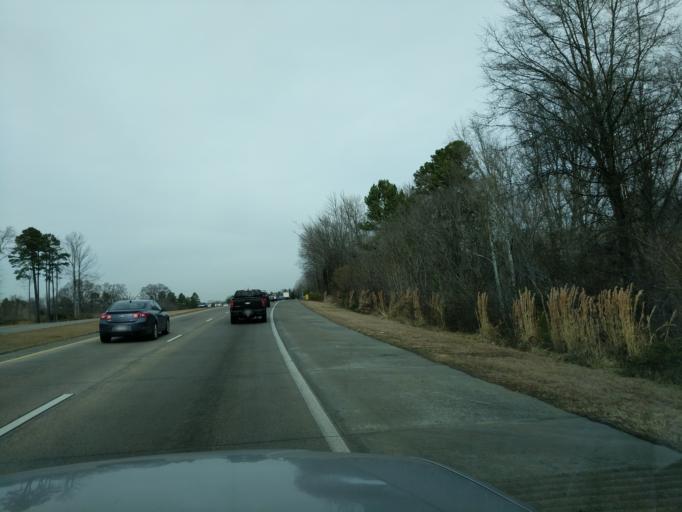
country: US
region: North Carolina
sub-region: Mecklenburg County
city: Charlotte
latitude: 35.2114
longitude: -80.9237
